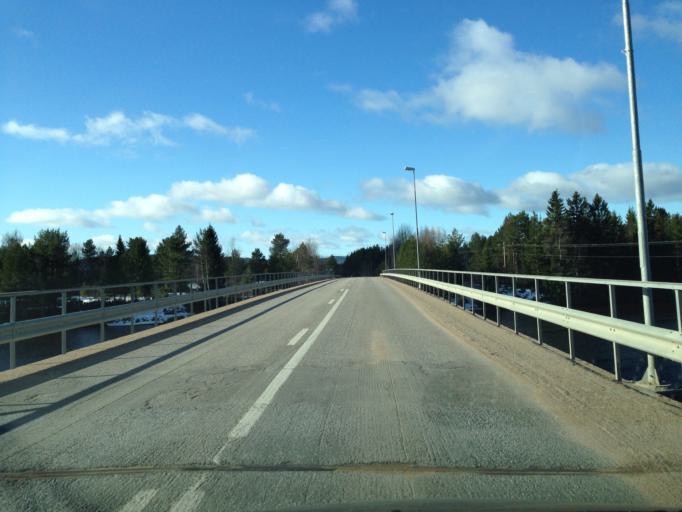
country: SE
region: Jaemtland
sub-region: Harjedalens Kommun
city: Sveg
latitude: 62.0469
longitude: 14.6490
